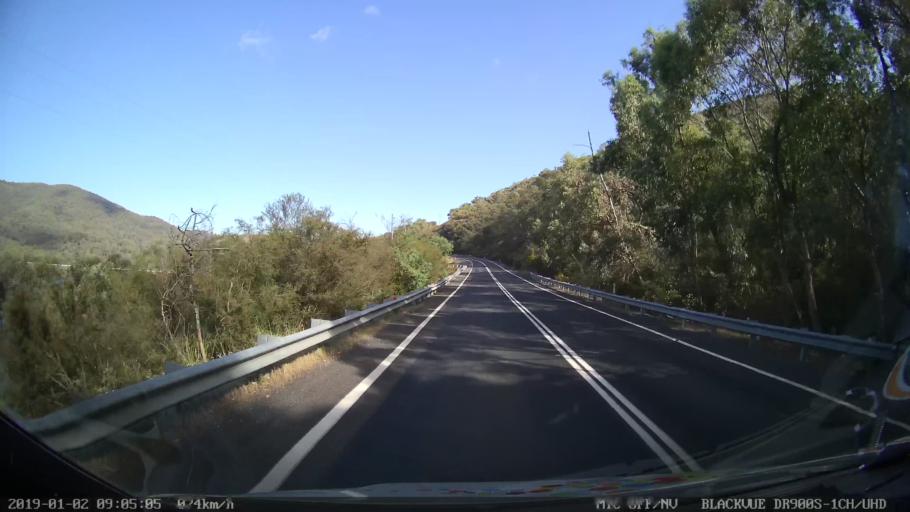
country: AU
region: New South Wales
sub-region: Tumut Shire
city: Tumut
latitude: -35.5631
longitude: 148.3128
